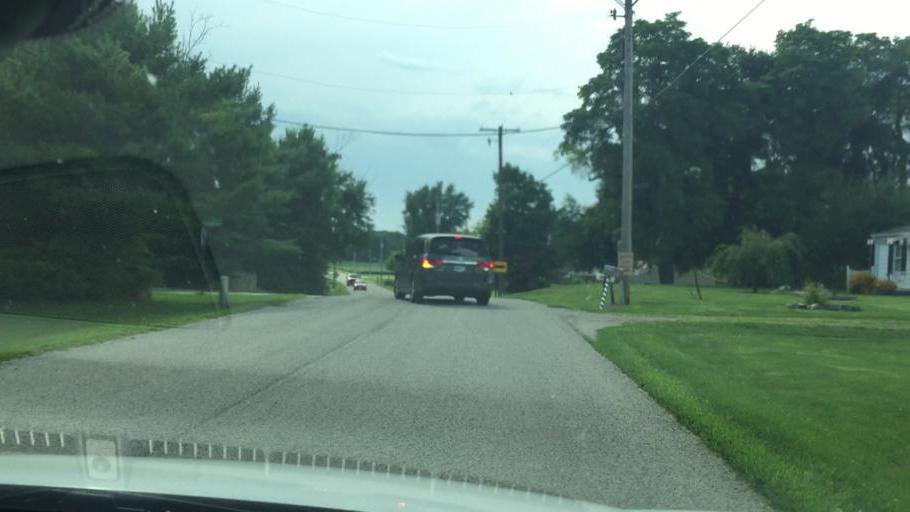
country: US
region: Ohio
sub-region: Clark County
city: Lisbon
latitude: 39.9453
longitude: -83.5982
